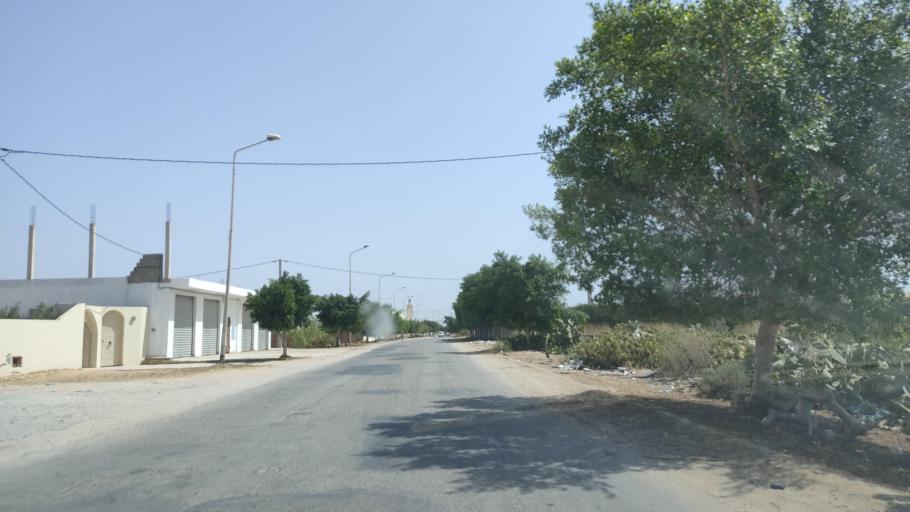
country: TN
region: Safaqis
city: Sfax
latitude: 34.6695
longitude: 10.7127
